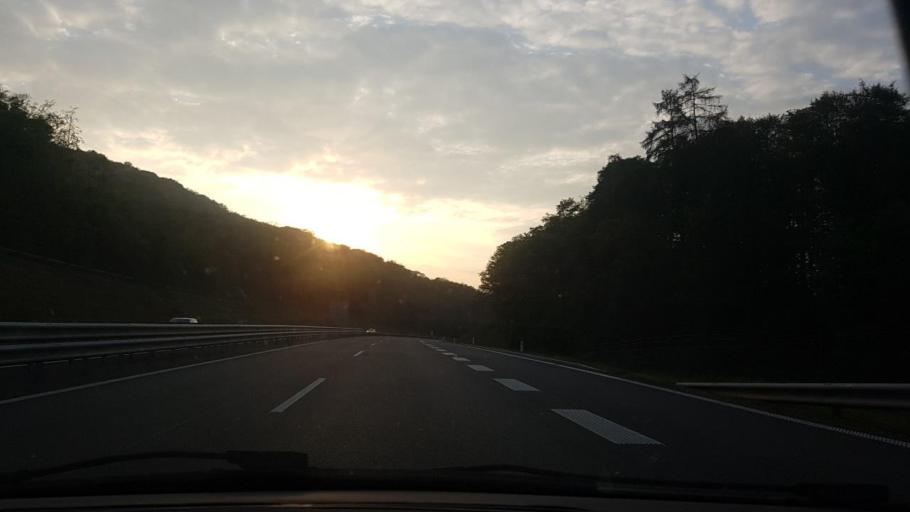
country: SI
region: Brezice
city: Brezice
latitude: 45.8930
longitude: 15.5937
